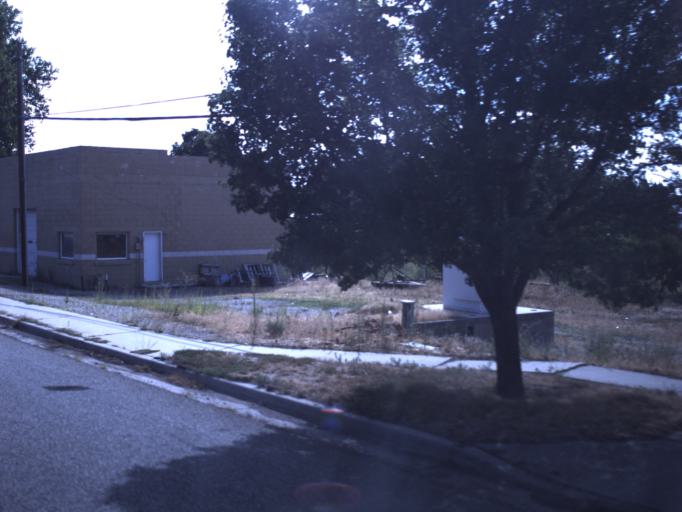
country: US
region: Utah
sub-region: Box Elder County
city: Perry
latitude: 41.4658
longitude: -112.0330
